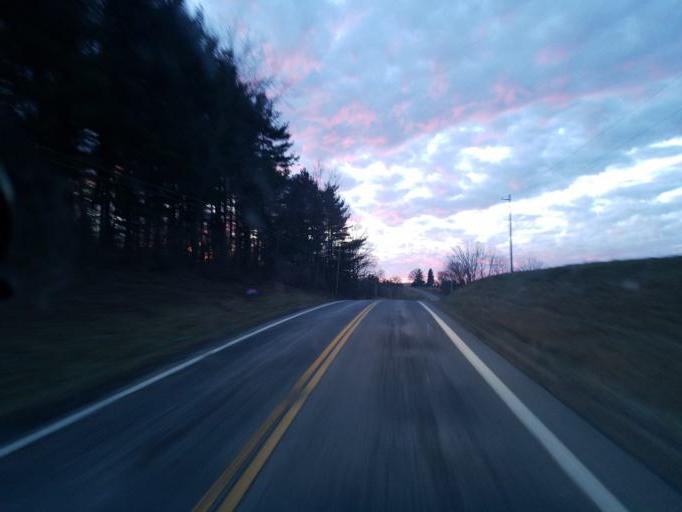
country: US
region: Ohio
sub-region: Knox County
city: Oak Hill
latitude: 40.2863
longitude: -82.2505
